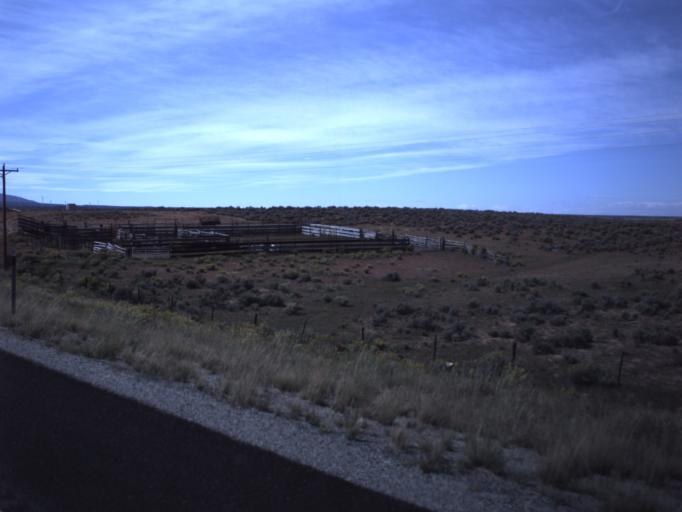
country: US
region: Utah
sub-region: San Juan County
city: Monticello
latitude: 37.8729
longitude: -109.2746
